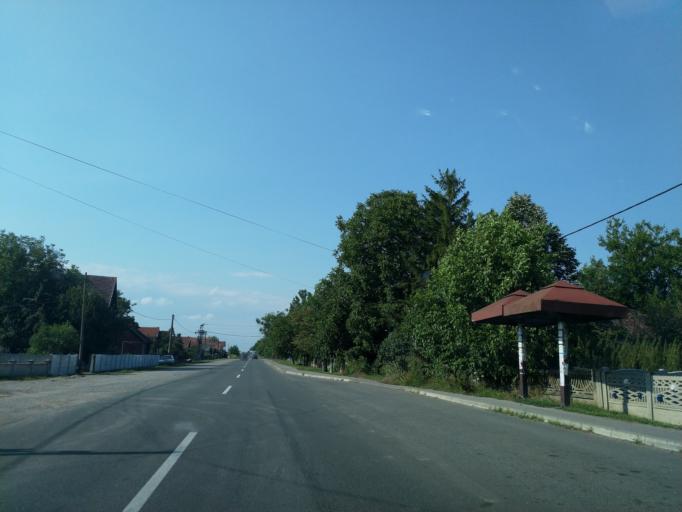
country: RS
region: Central Serbia
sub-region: Pomoravski Okrug
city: Paracin
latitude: 43.8037
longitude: 21.4216
